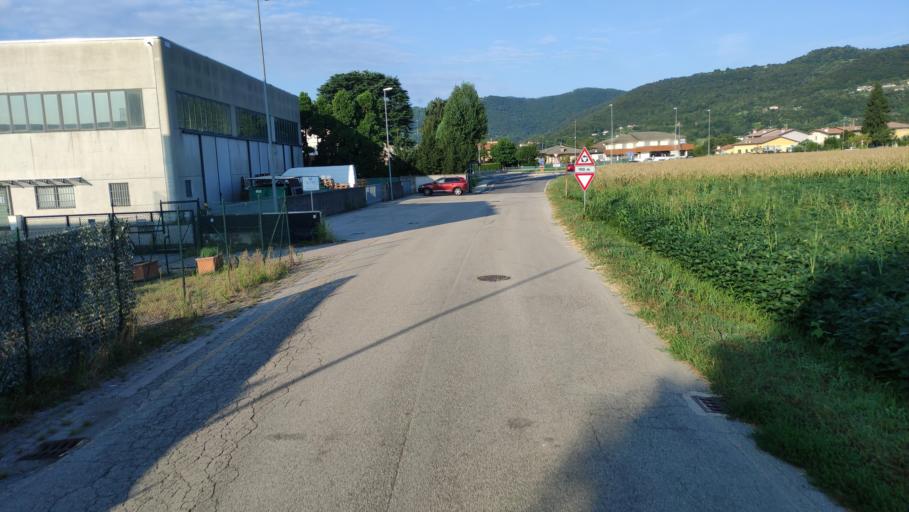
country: IT
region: Veneto
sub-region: Provincia di Vicenza
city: Isola Vicentina
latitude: 45.6382
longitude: 11.4372
